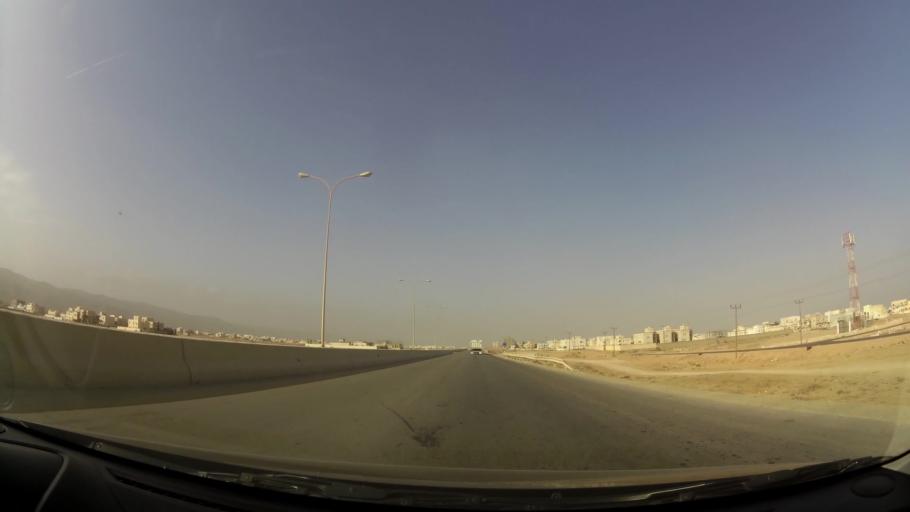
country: OM
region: Zufar
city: Salalah
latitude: 17.0207
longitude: 54.0143
